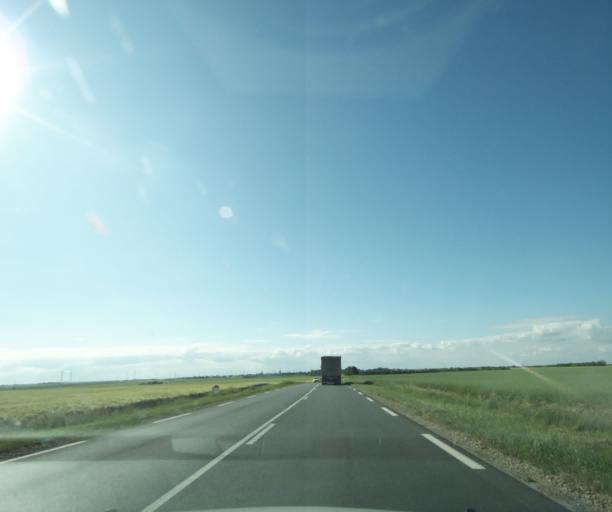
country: FR
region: Centre
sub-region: Departement d'Eure-et-Loir
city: Janville
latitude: 48.2487
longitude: 1.7708
